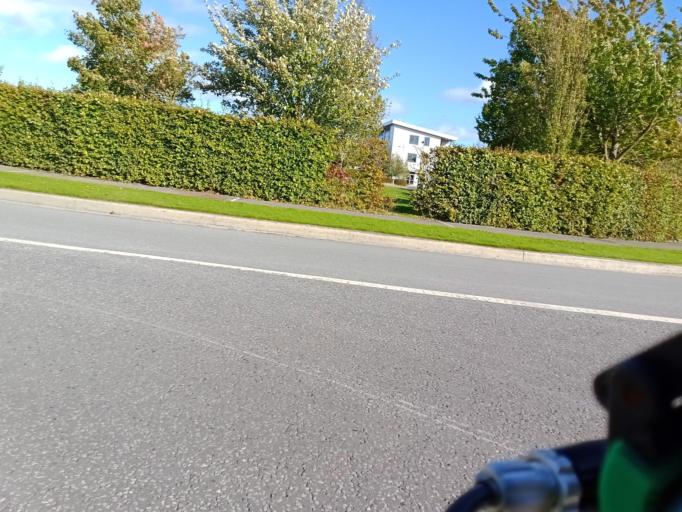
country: IE
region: Leinster
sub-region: Kilkenny
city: Kilkenny
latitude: 52.6343
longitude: -7.2380
